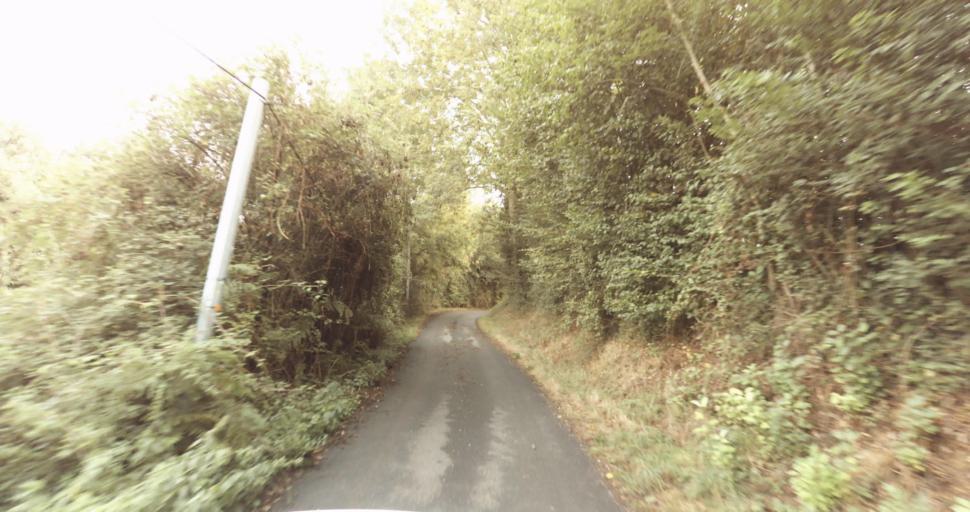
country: FR
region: Lower Normandy
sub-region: Departement de l'Orne
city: Trun
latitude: 48.9001
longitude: 0.1010
